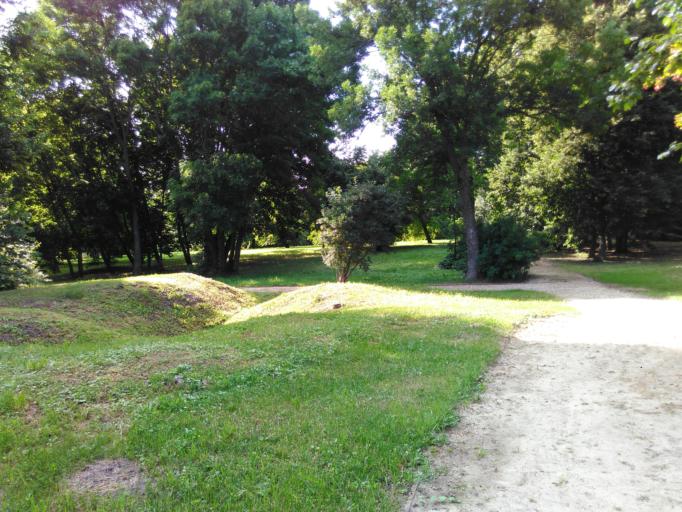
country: RU
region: Penza
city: Lermontovo
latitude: 52.9629
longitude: 43.6713
